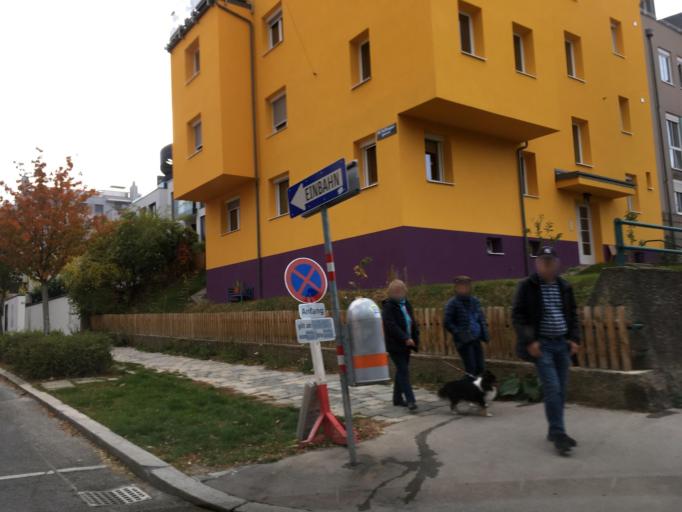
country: AT
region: Vienna
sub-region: Wien Stadt
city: Vienna
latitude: 48.2446
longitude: 16.3359
